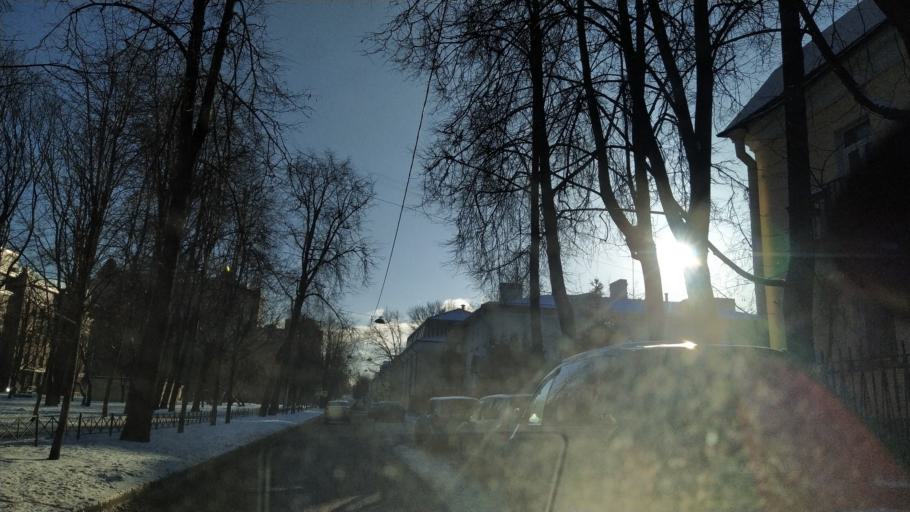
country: RU
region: St.-Petersburg
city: Novaya Derevnya
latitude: 59.9874
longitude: 30.2840
